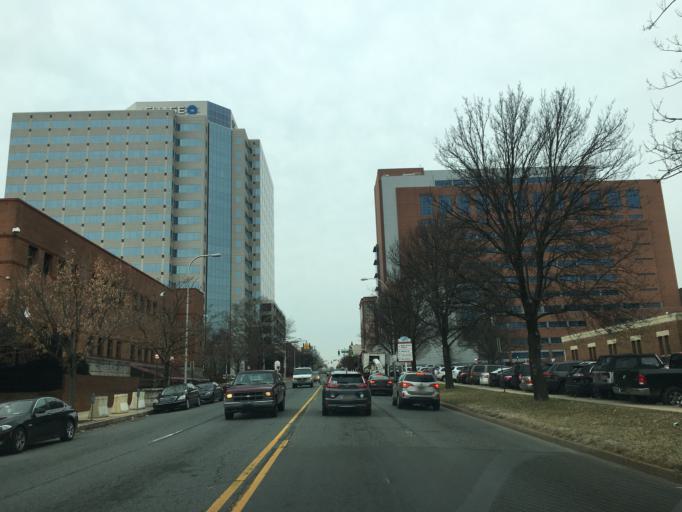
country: US
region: Delaware
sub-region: New Castle County
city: Wilmington
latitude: 39.7389
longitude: -75.5475
